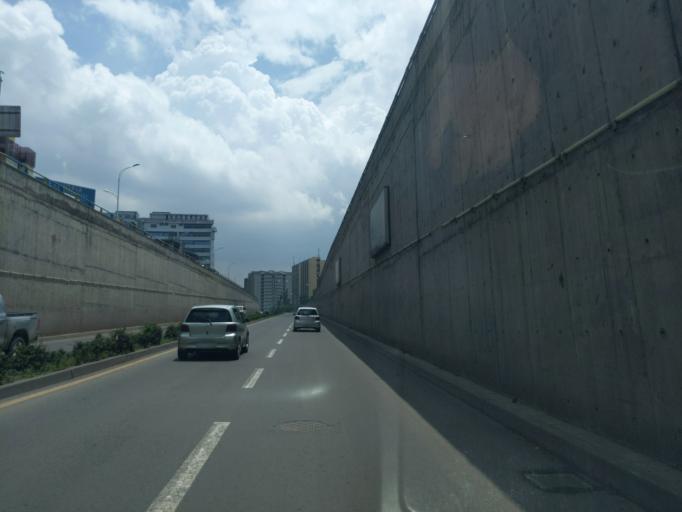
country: ET
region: Adis Abeba
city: Addis Ababa
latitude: 9.0045
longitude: 38.7681
